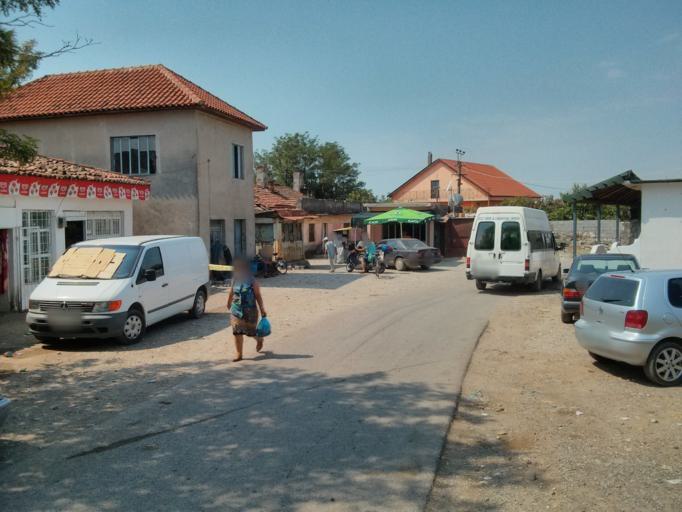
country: AL
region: Shkoder
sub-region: Rrethi i Malesia e Madhe
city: Gruemire
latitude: 42.1215
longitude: 19.5603
